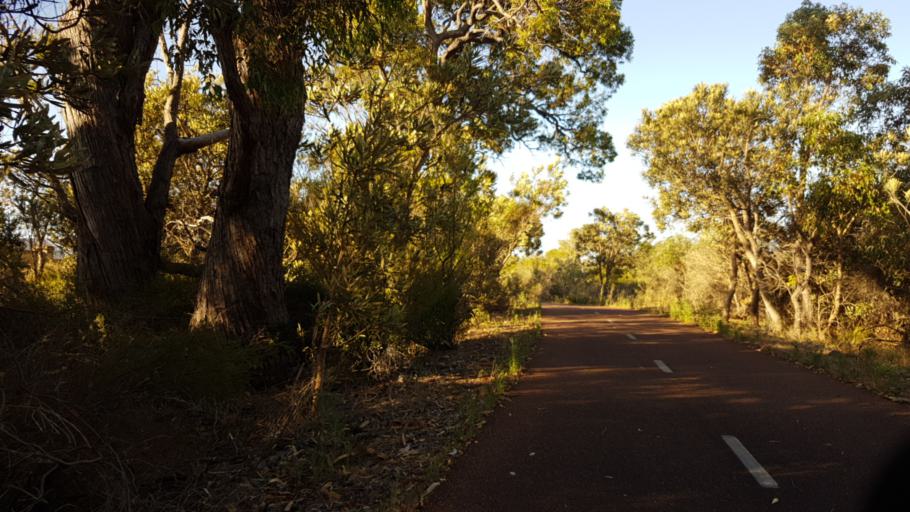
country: AU
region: Western Australia
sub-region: Kwinana
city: Bertram
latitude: -32.2541
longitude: 115.8520
